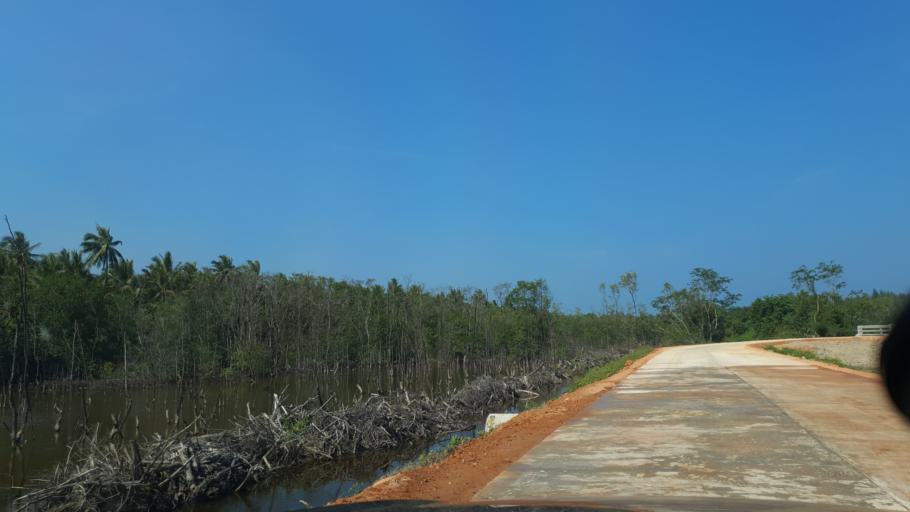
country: TH
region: Surat Thani
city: Tha Chana
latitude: 9.5937
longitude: 99.2078
